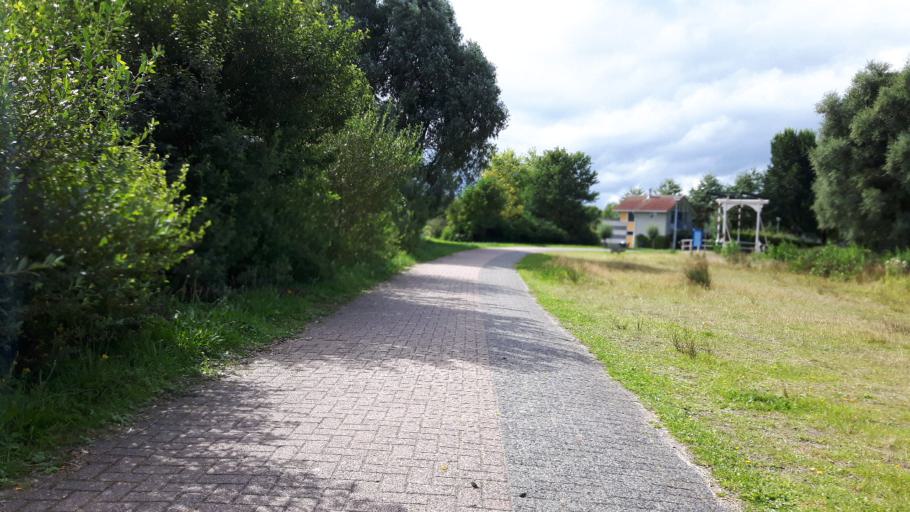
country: NL
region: Groningen
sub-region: Gemeente Appingedam
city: Appingedam
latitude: 53.2692
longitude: 6.8411
